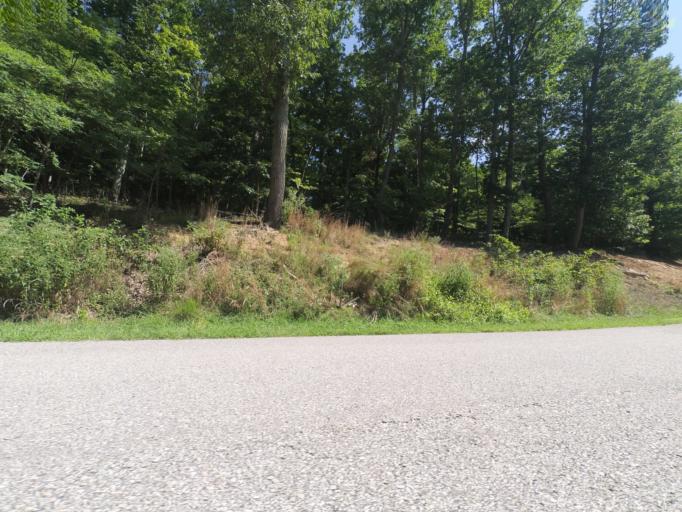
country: US
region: West Virginia
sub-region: Cabell County
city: Huntington
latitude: 38.3860
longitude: -82.4618
